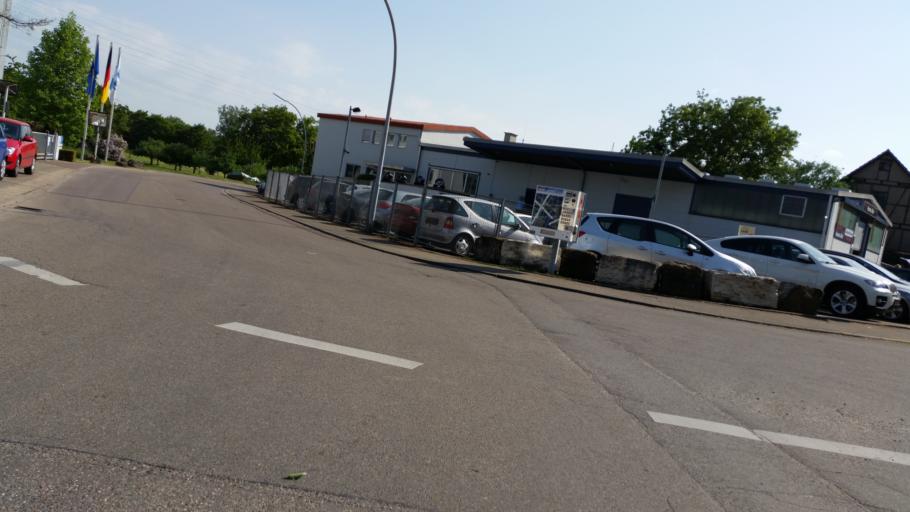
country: DE
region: Baden-Wuerttemberg
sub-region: Regierungsbezirk Stuttgart
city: Pleidelsheim
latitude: 48.9622
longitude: 9.1889
